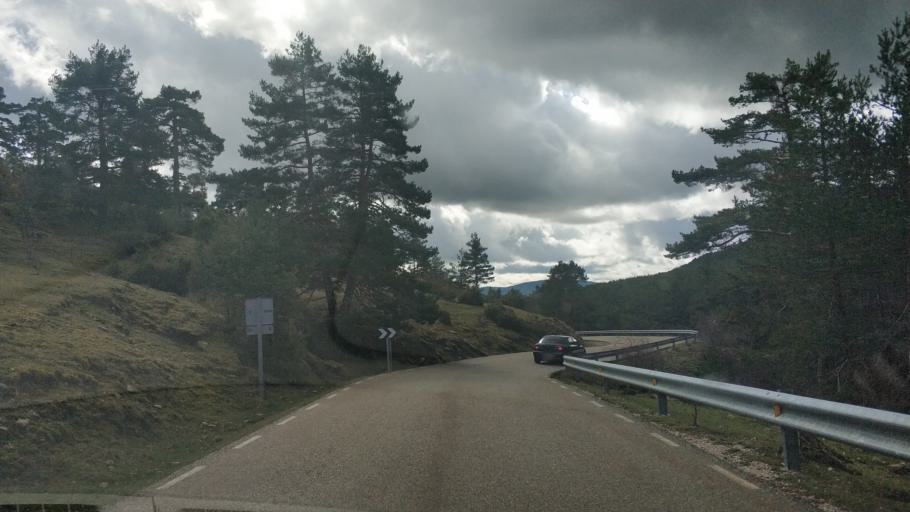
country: ES
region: Castille and Leon
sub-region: Provincia de Burgos
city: Neila
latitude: 42.0354
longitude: -3.0055
